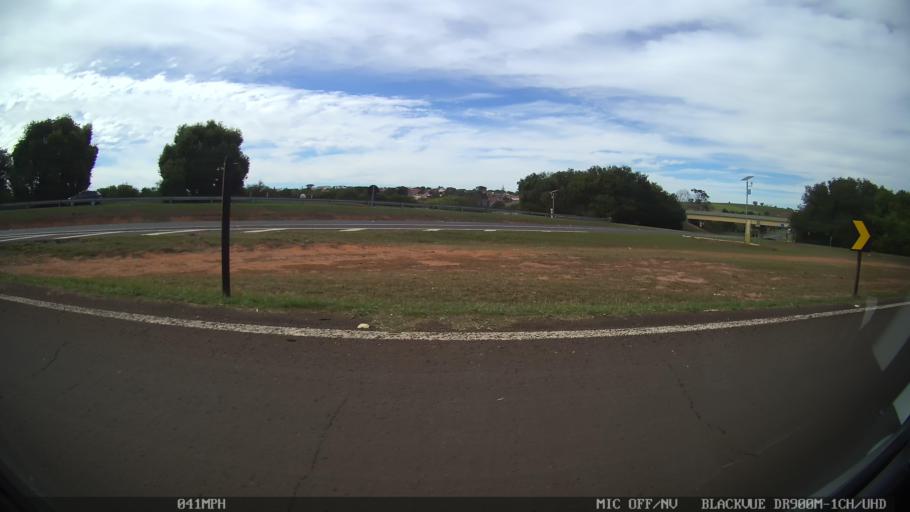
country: BR
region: Sao Paulo
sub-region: Santa Adelia
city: Santa Adelia
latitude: -21.3708
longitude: -48.7505
